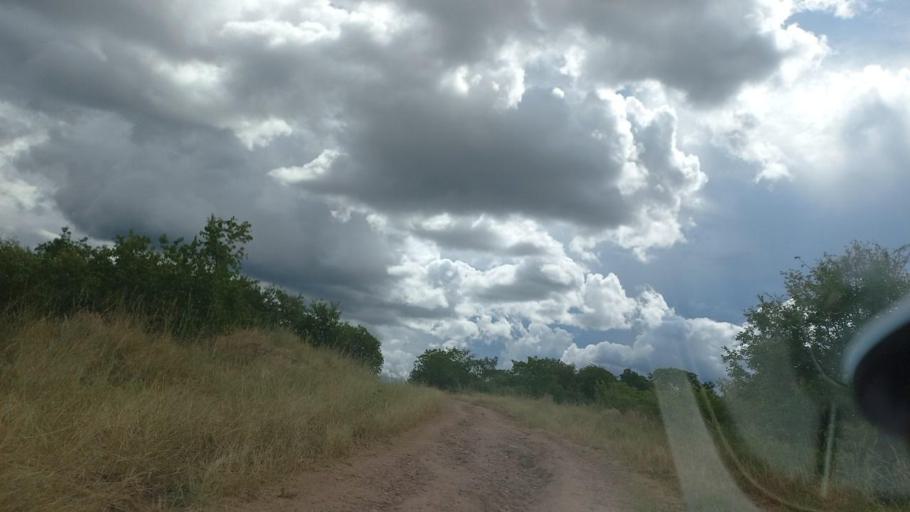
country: ZM
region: Lusaka
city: Luangwa
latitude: -15.6413
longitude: 30.3826
